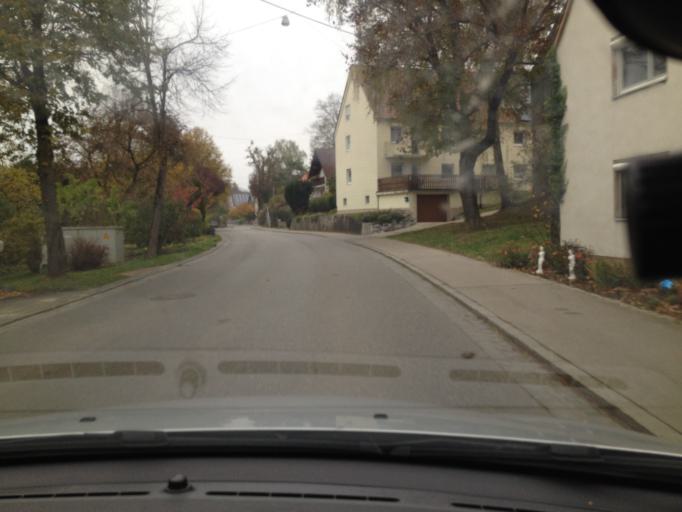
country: DE
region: Bavaria
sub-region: Swabia
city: Langerringen
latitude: 48.1438
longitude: 10.7587
